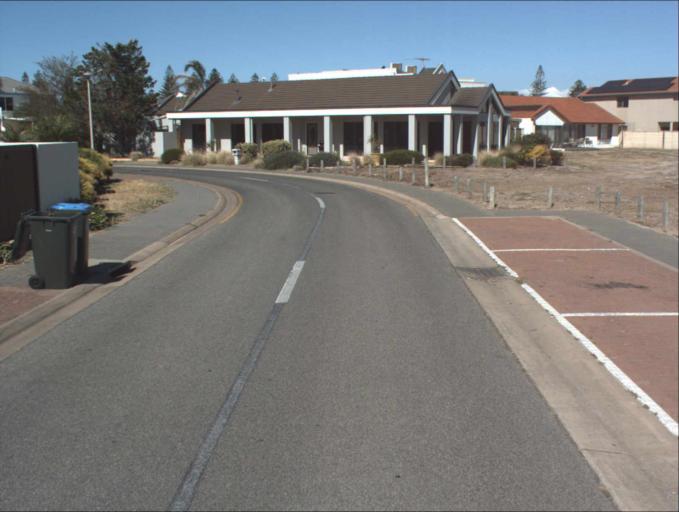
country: AU
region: South Australia
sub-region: Port Adelaide Enfield
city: Birkenhead
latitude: -34.7962
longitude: 138.4873
